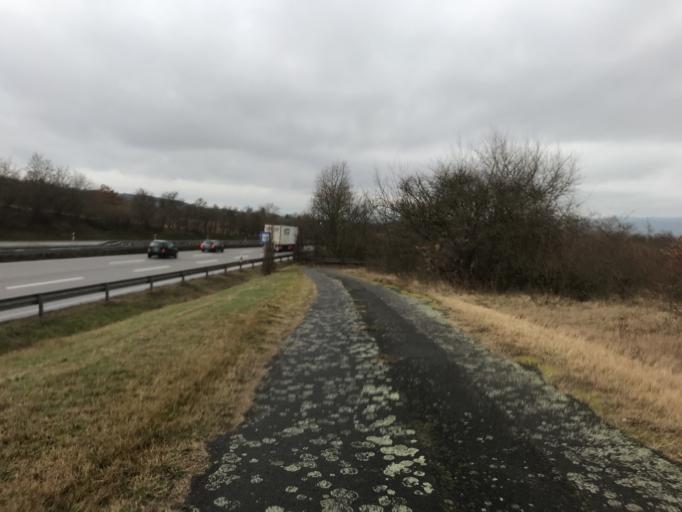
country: DE
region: Rheinland-Pfalz
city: Wackernheim
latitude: 49.9992
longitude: 8.1378
